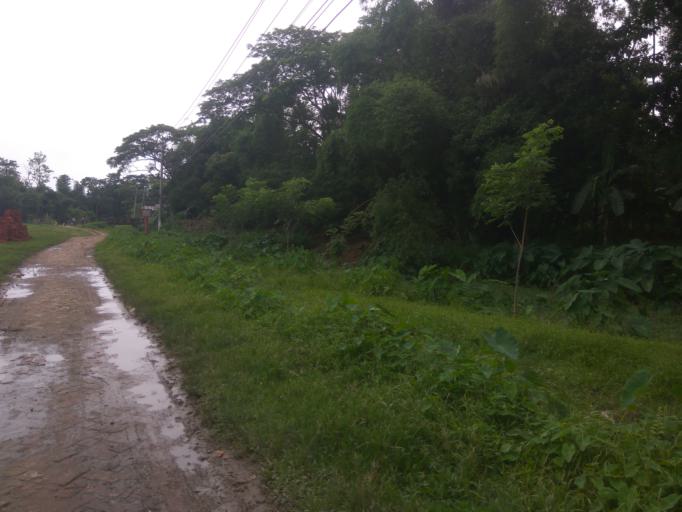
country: IN
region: Assam
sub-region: Karimganj
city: Karimganj
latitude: 24.8587
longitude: 92.1889
